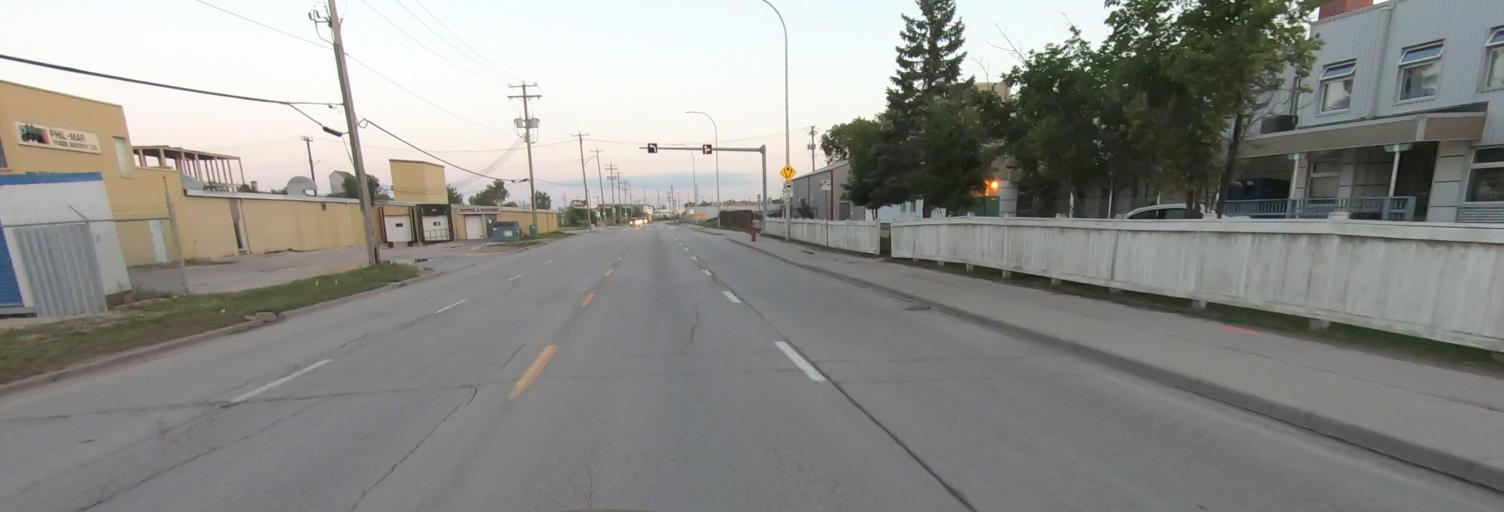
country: CA
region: Manitoba
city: Winnipeg
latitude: 49.8939
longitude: -97.1046
